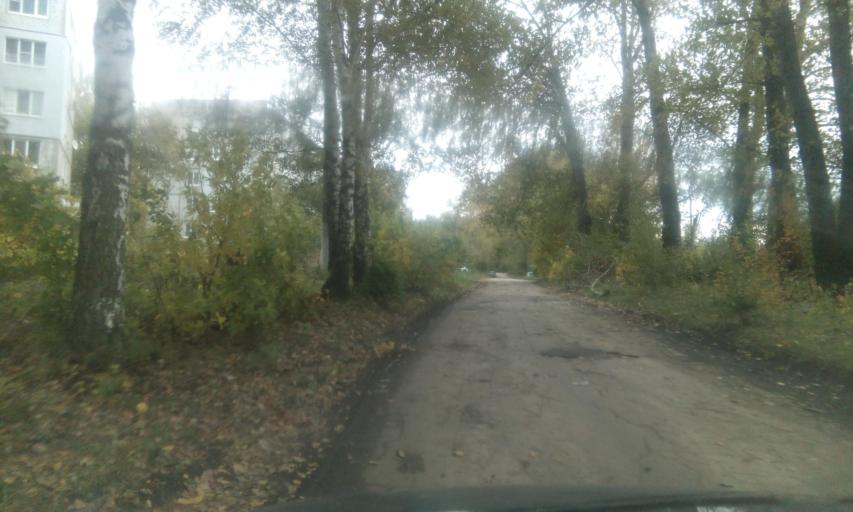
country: RU
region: Tula
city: Gritsovskiy
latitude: 54.1333
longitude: 38.1566
